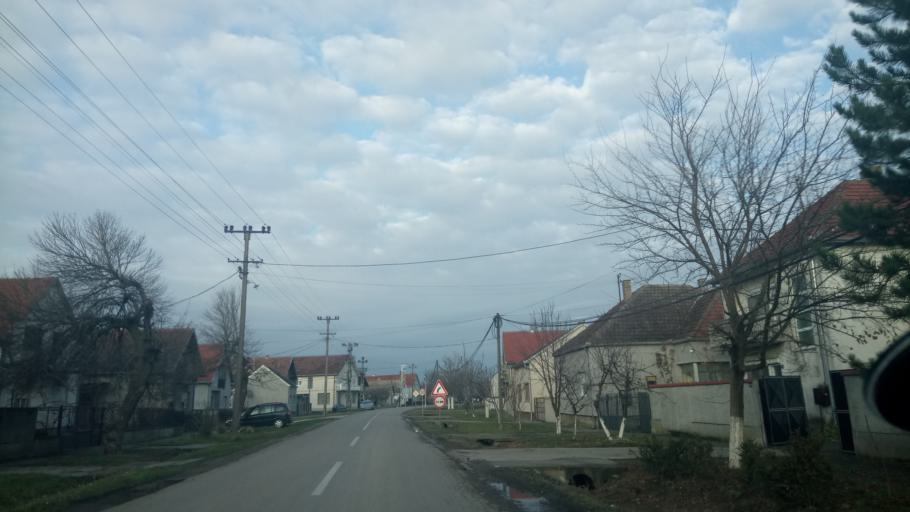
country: RS
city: Vojka
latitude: 44.9354
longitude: 20.1656
